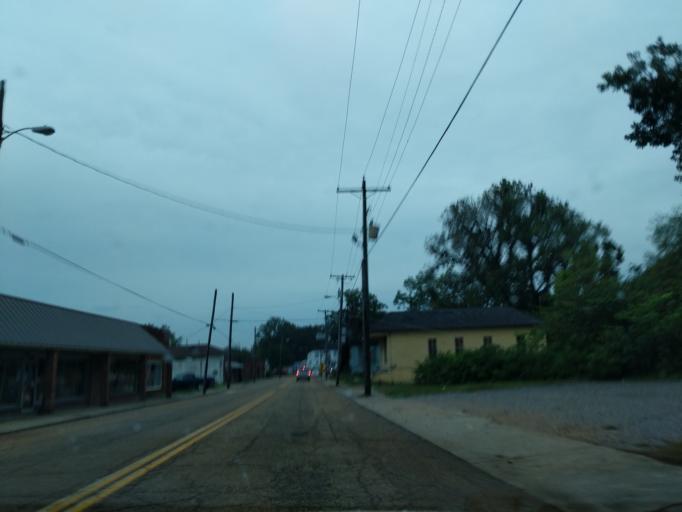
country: US
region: Mississippi
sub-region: Warren County
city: Vicksburg
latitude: 32.3372
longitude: -90.8865
